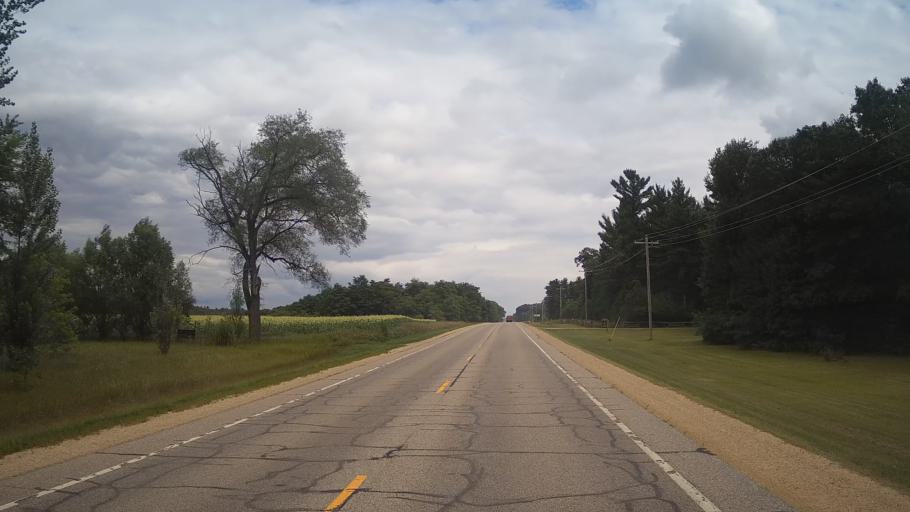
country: US
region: Wisconsin
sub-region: Waushara County
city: Wautoma
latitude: 44.0684
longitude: -89.3317
